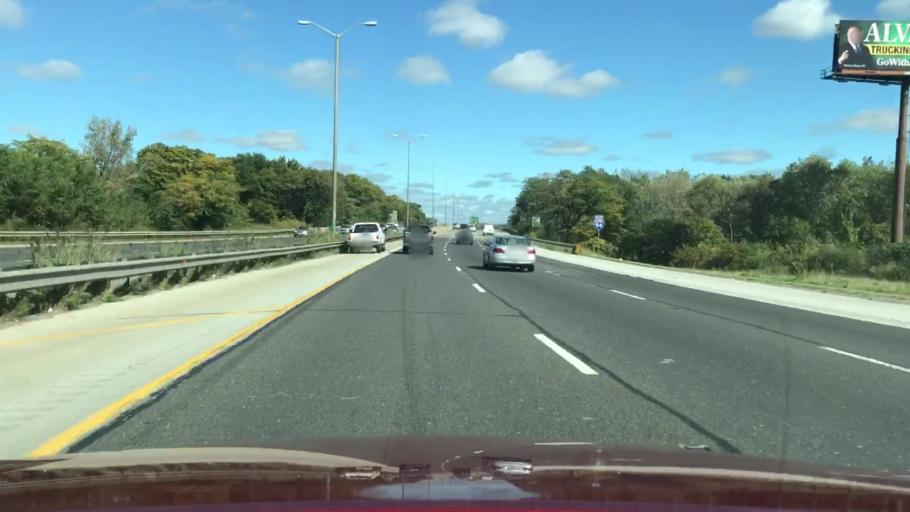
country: US
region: Illinois
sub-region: Cook County
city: South Holland
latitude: 41.6051
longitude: -87.5828
